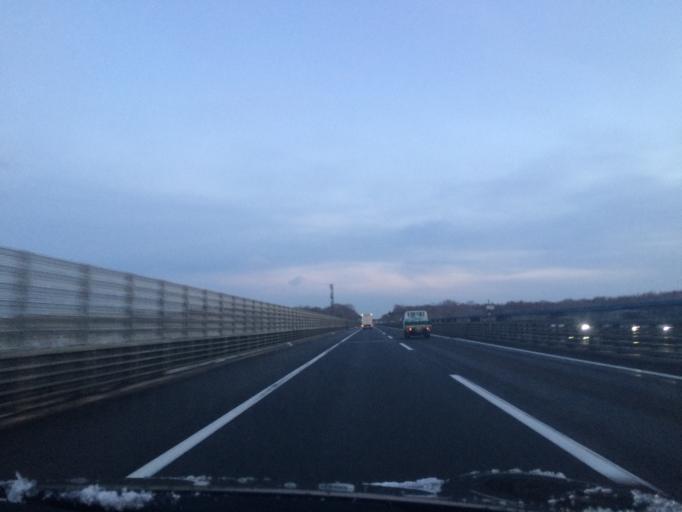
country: JP
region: Hokkaido
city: Chitose
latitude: 42.8196
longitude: 141.6178
